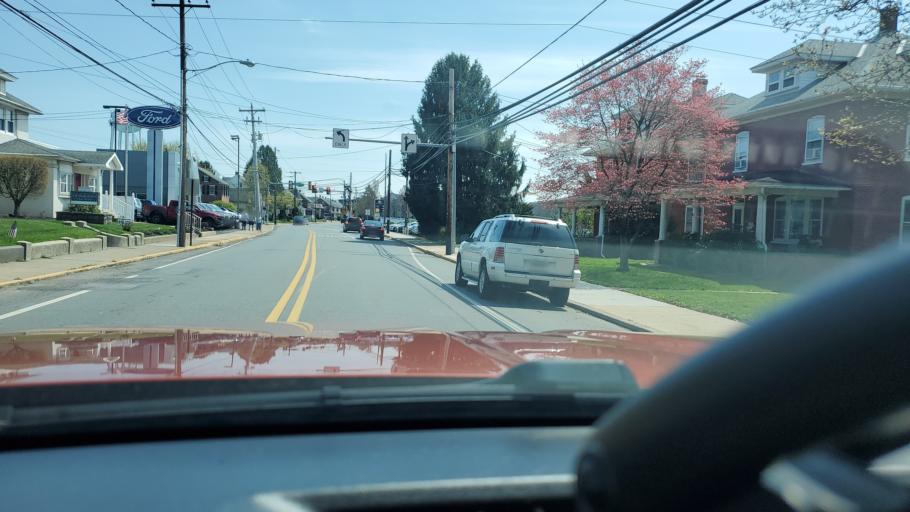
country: US
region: Pennsylvania
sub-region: Montgomery County
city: Red Hill
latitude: 40.3783
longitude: -75.4839
